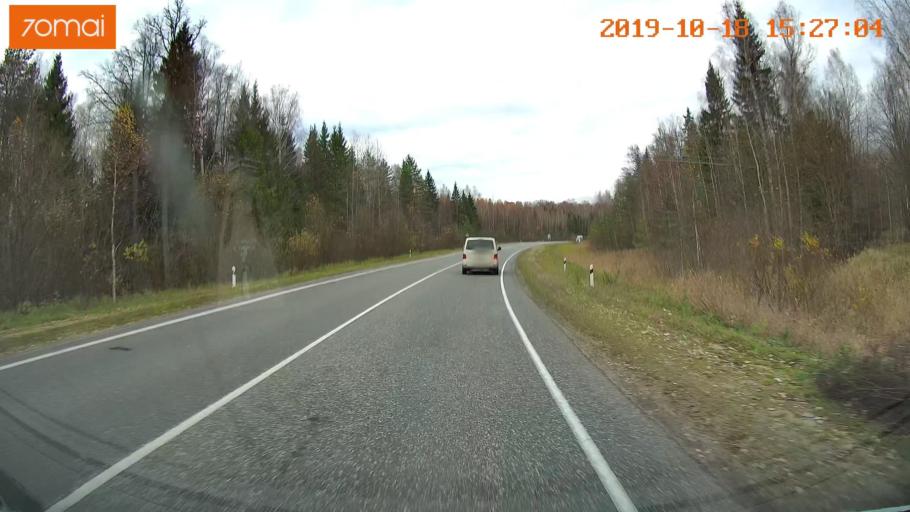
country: RU
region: Vladimir
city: Anopino
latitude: 55.7489
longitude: 40.6735
